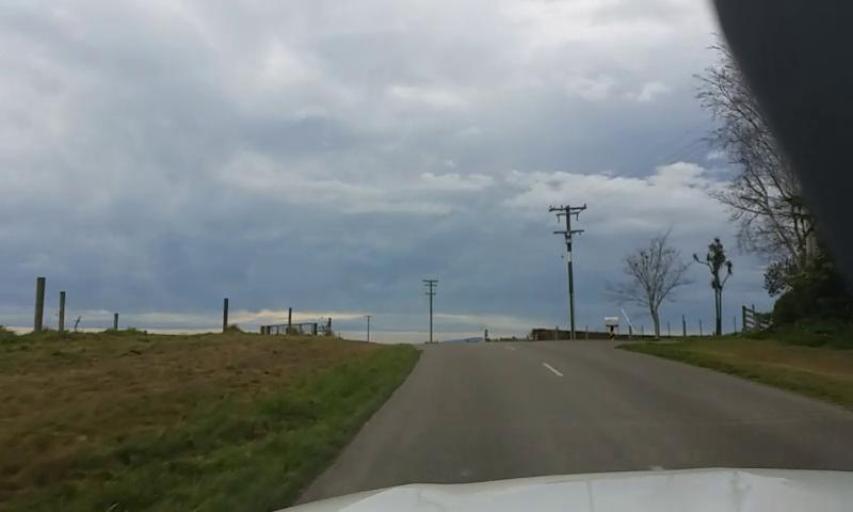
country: NZ
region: Canterbury
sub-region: Waimakariri District
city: Kaiapoi
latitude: -43.2965
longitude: 172.4763
